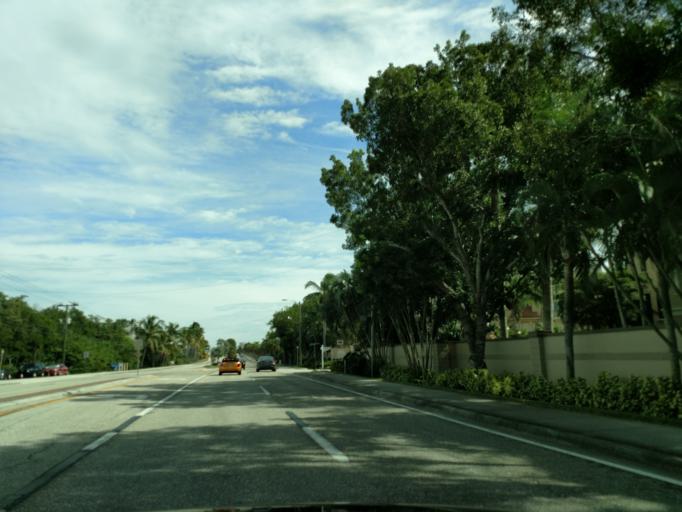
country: US
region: Florida
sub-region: Lee County
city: Bonita Springs
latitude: 26.3304
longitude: -81.8413
